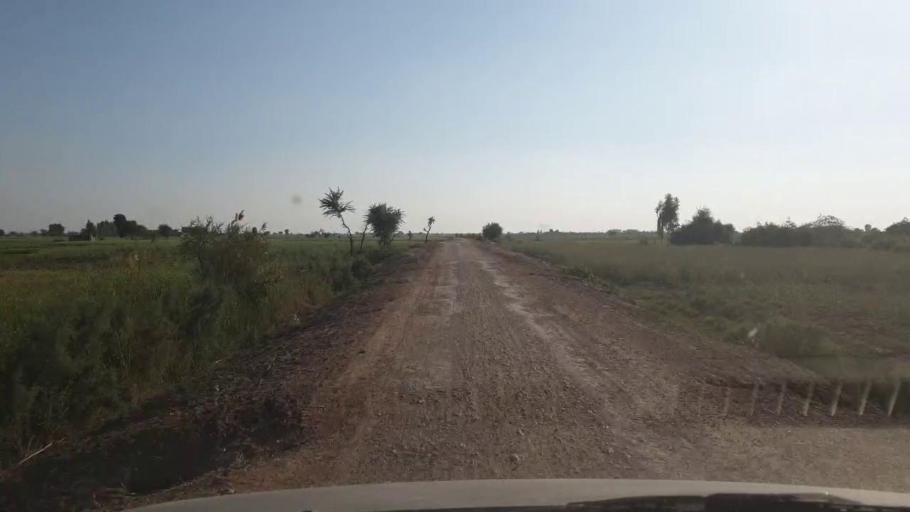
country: PK
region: Sindh
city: Mirwah Gorchani
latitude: 25.3662
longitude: 69.0968
